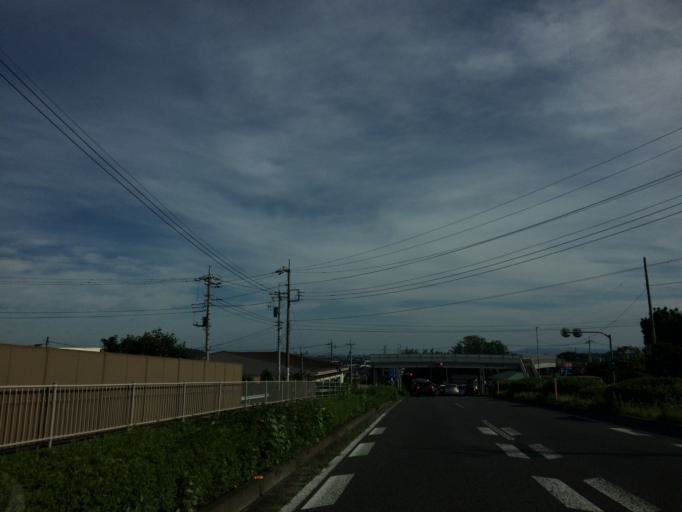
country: JP
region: Gunma
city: Shibukawa
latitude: 36.4856
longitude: 138.9994
